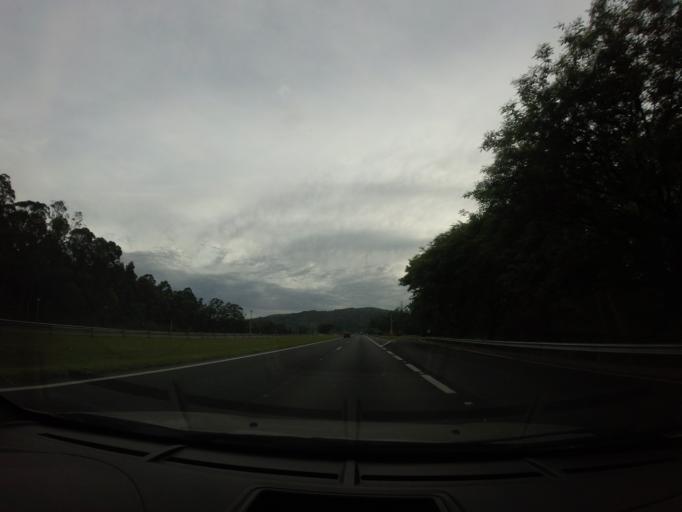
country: BR
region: Sao Paulo
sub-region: Valinhos
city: Valinhos
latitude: -22.9130
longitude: -46.9586
